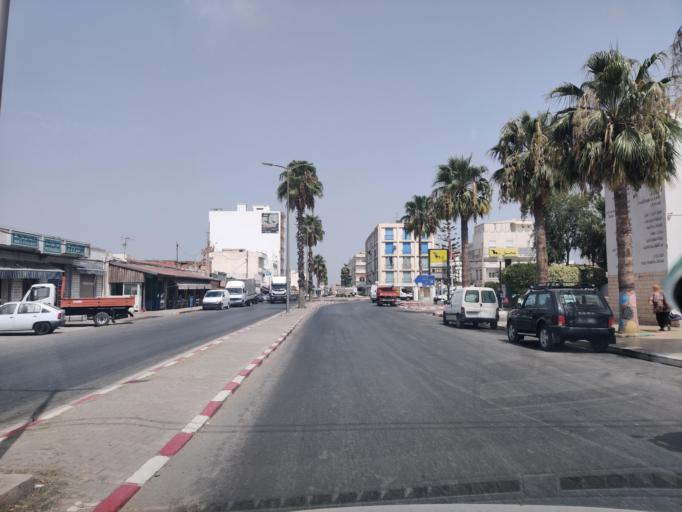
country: TN
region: Nabul
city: Bu `Urqub
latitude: 36.5977
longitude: 10.4996
